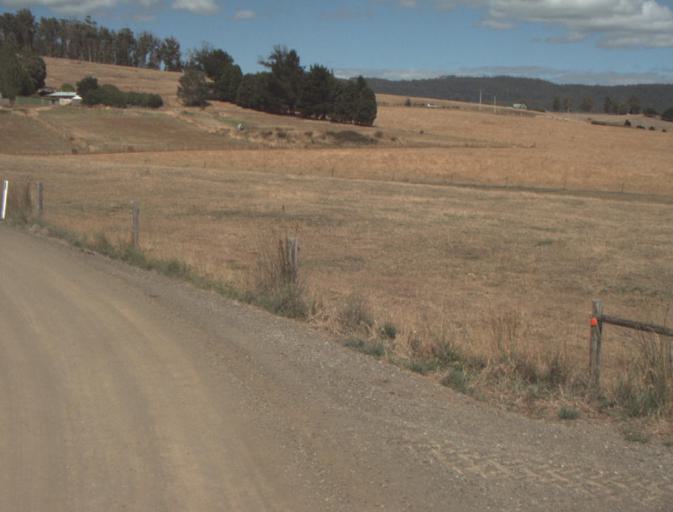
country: AU
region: Tasmania
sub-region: Launceston
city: Mayfield
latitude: -41.2181
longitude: 147.1588
